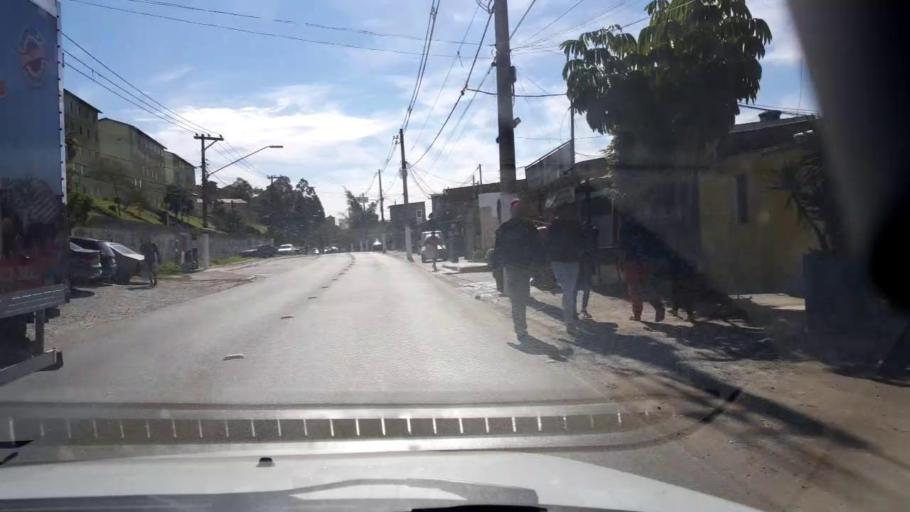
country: BR
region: Sao Paulo
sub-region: Ferraz De Vasconcelos
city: Ferraz de Vasconcelos
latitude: -23.5711
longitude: -46.4155
